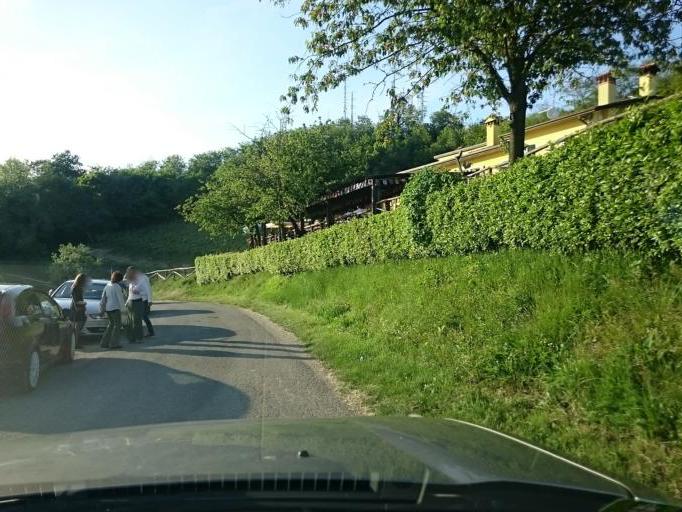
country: IT
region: Veneto
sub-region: Provincia di Padova
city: Galzignano
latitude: 45.2983
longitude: 11.7043
